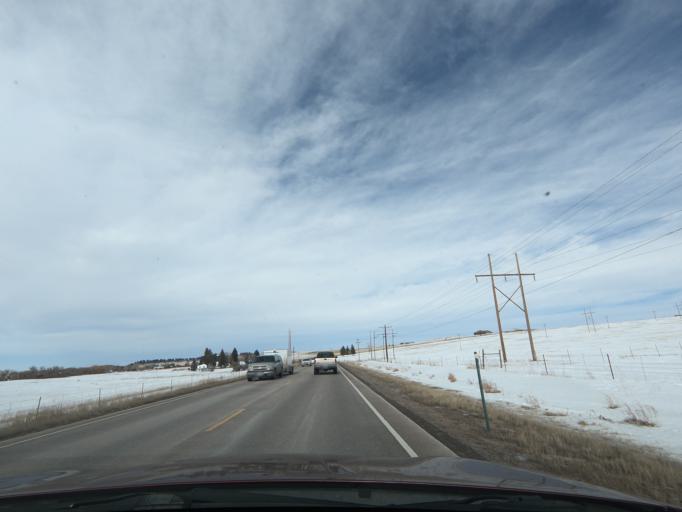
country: US
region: Colorado
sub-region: Elbert County
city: Elizabeth
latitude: 39.2334
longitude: -104.6972
